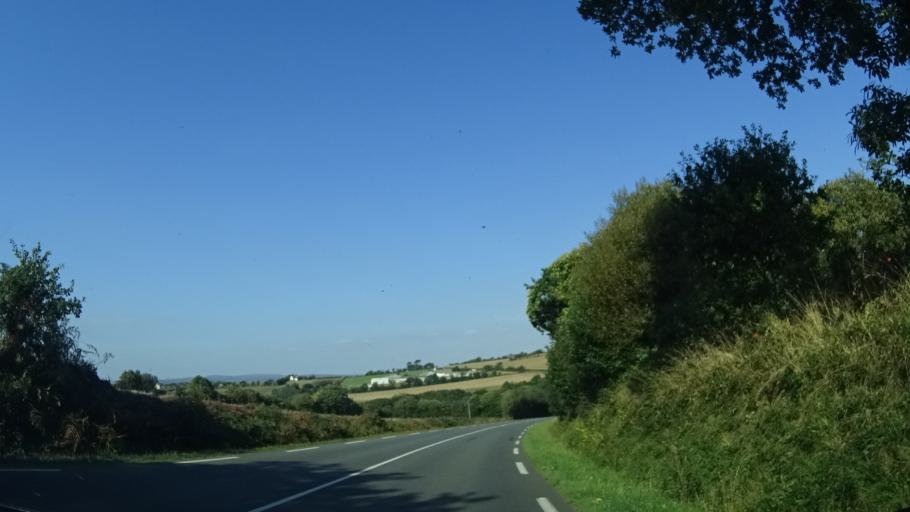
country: FR
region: Brittany
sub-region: Departement du Finistere
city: Plonevez-Porzay
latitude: 48.1087
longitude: -4.2446
